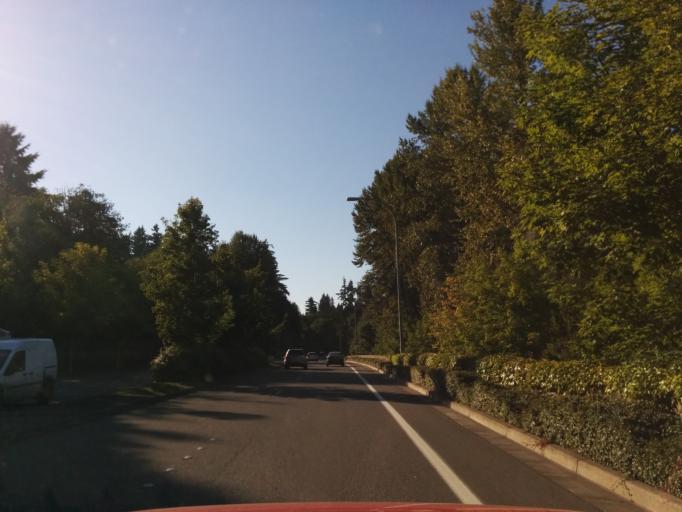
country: US
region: Washington
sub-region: King County
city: Redmond
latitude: 47.6585
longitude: -122.1220
